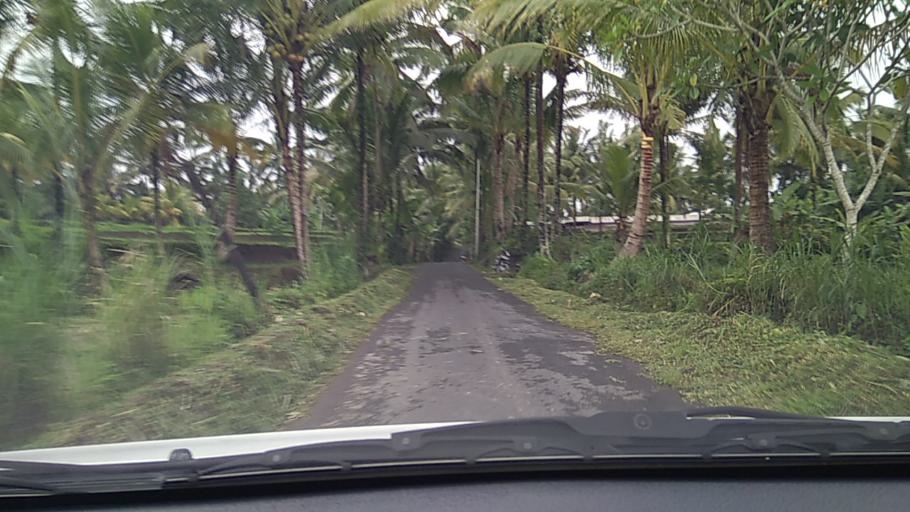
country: ID
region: Bali
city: Banjar Dujung Kaja
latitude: -8.4048
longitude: 115.2906
